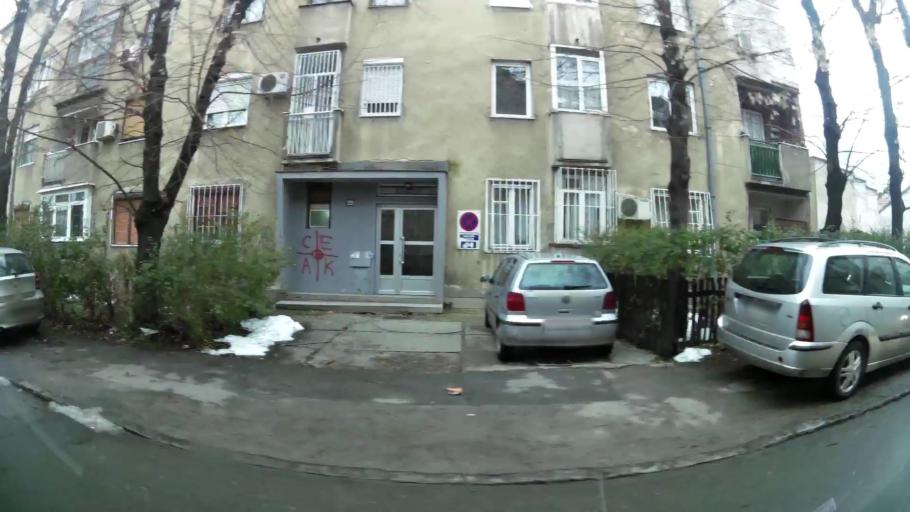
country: RS
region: Central Serbia
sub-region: Belgrade
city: Savski Venac
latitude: 44.7961
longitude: 20.4468
